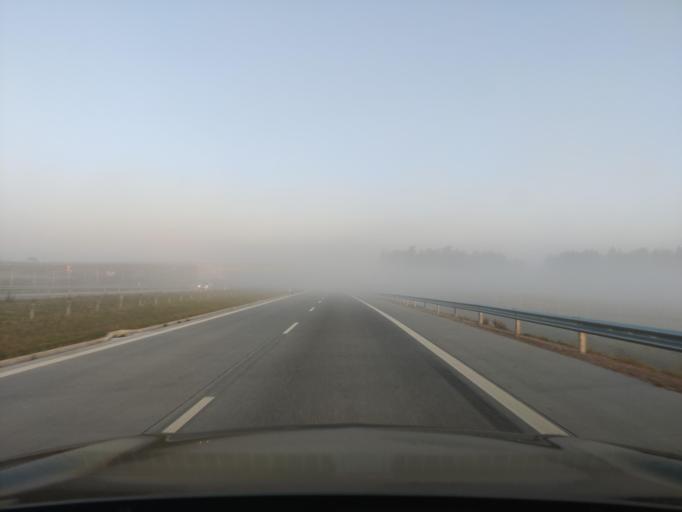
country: PL
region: Masovian Voivodeship
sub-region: Powiat mlawski
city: Wisniewo
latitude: 53.0010
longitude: 20.3437
